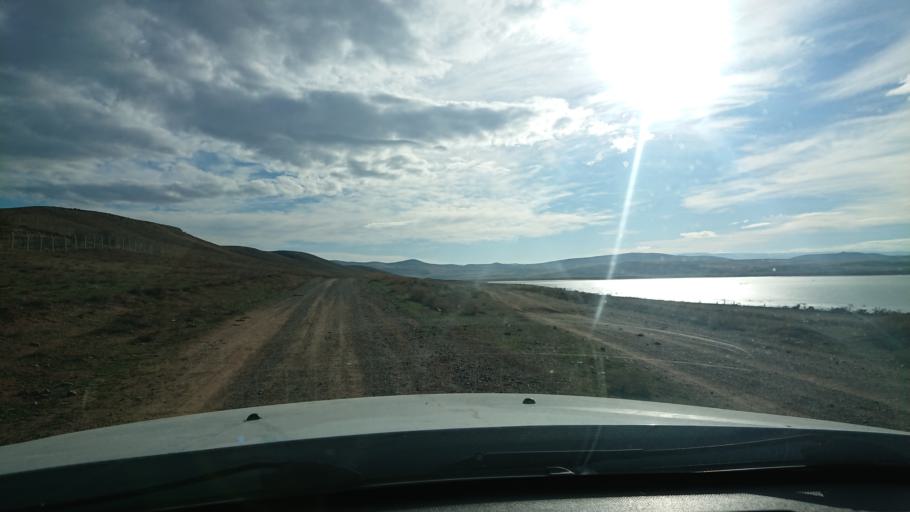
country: TR
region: Aksaray
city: Sariyahsi
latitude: 39.0495
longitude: 33.9741
